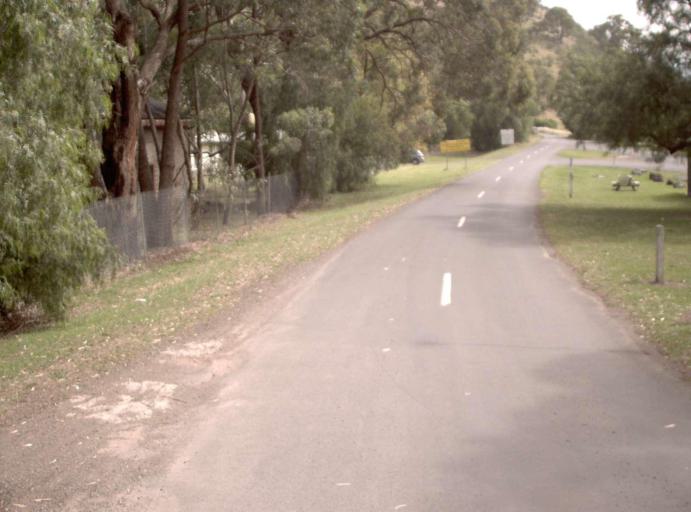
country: AU
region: Victoria
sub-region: Wellington
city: Heyfield
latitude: -37.6281
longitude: 146.6230
